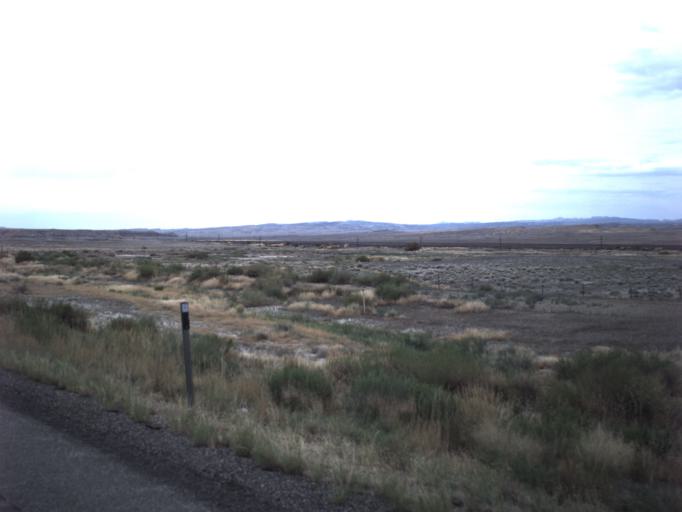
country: US
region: Utah
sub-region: Carbon County
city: East Carbon City
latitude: 39.3623
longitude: -110.3902
